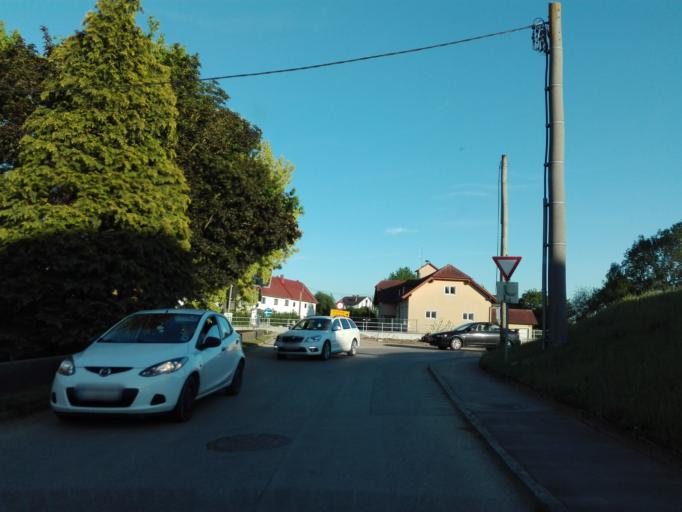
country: AT
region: Upper Austria
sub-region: Politischer Bezirk Urfahr-Umgebung
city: Feldkirchen an der Donau
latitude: 48.3107
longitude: 14.0046
